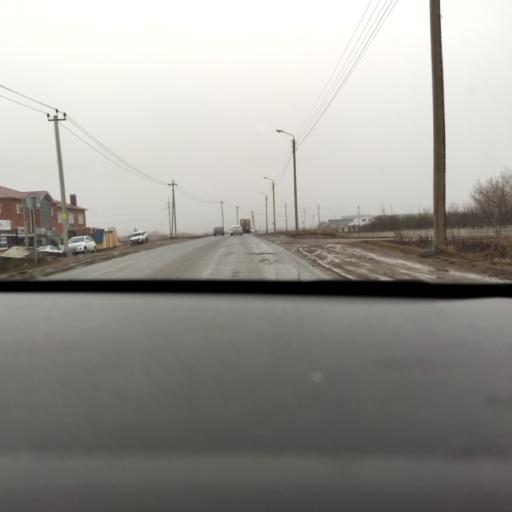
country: RU
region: Tatarstan
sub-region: Chistopol'skiy Rayon
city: Chistopol'
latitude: 55.3462
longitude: 50.6593
